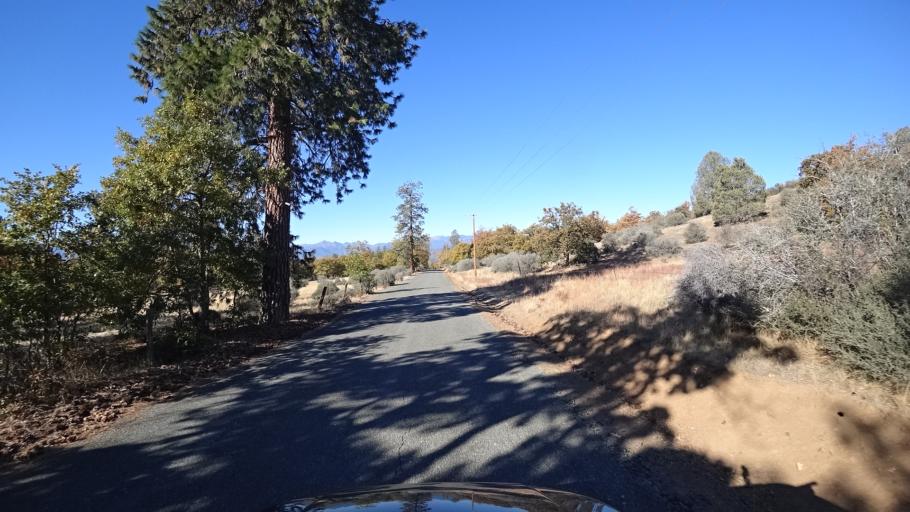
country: US
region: California
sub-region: Siskiyou County
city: Yreka
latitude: 41.5777
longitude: -122.8091
